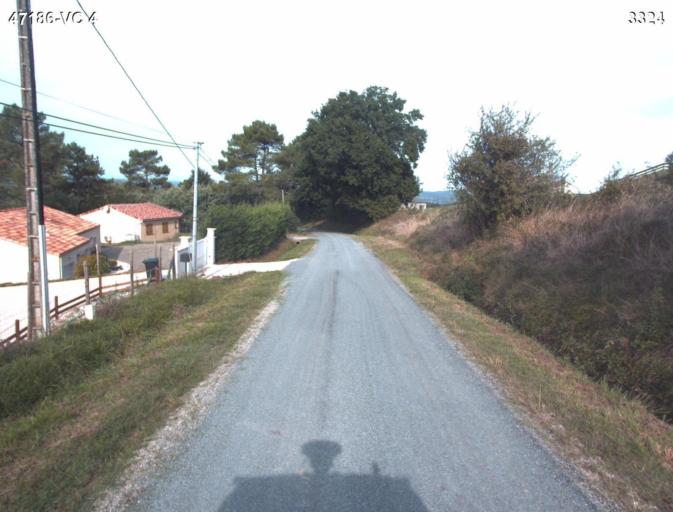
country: FR
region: Aquitaine
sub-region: Departement du Lot-et-Garonne
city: Port-Sainte-Marie
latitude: 44.2013
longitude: 0.4447
